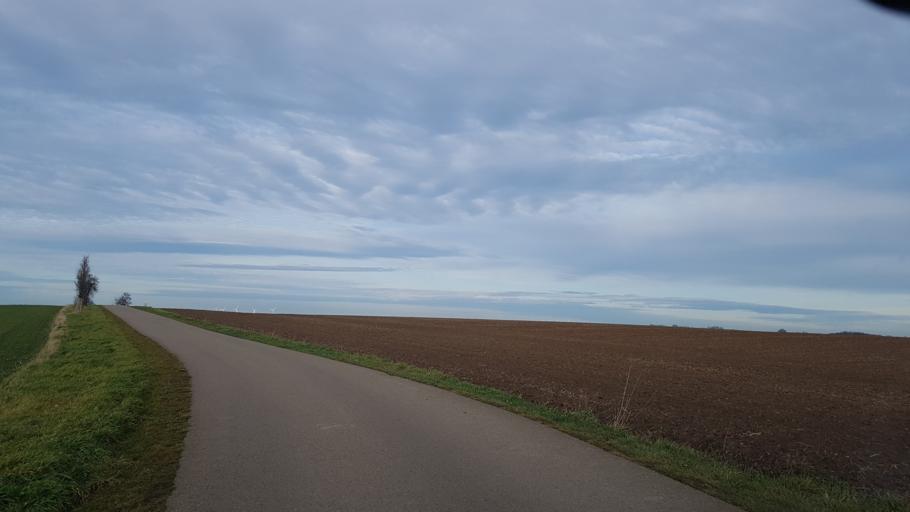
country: DE
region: Saxony
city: Ostrau
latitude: 51.1756
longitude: 13.1772
